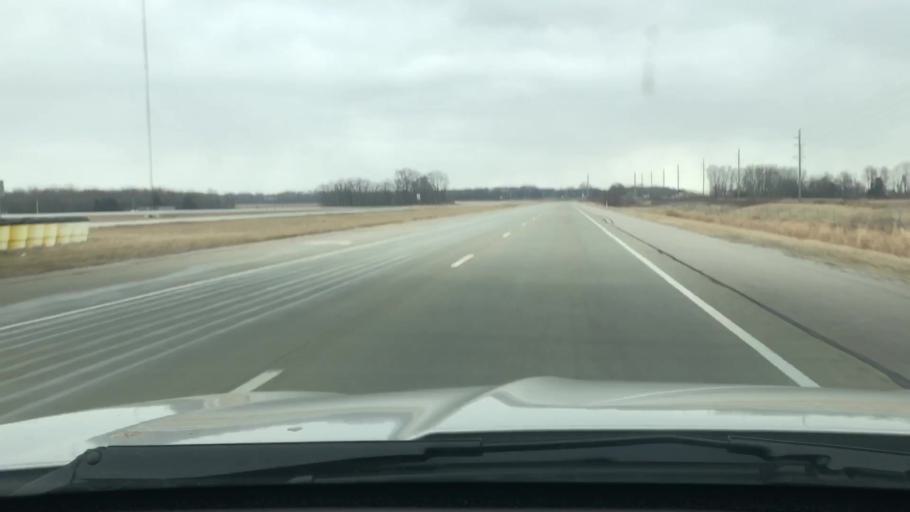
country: US
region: Indiana
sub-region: Carroll County
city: Delphi
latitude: 40.4997
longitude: -86.7330
